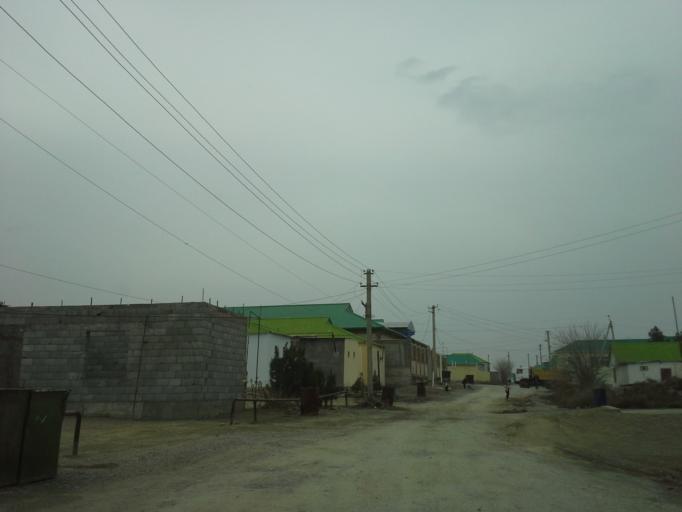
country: TM
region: Ahal
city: Abadan
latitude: 37.9783
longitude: 58.2243
